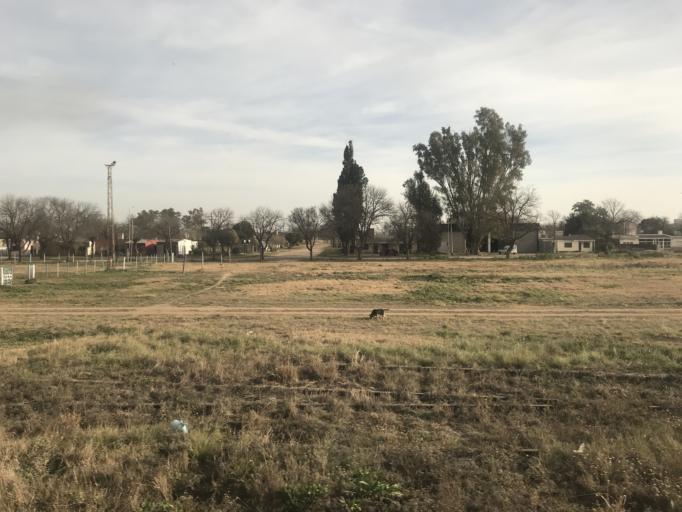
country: AR
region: Cordoba
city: Pilar
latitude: -31.6782
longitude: -63.8891
